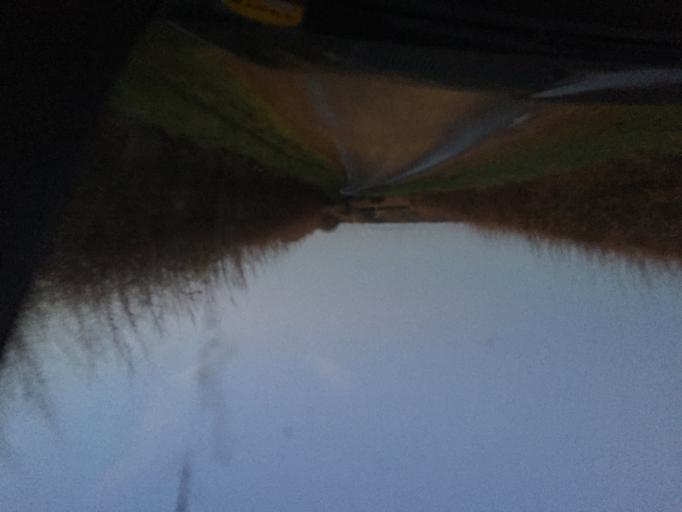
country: GB
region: England
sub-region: Northamptonshire
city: Silverstone
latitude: 52.0875
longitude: -1.0877
